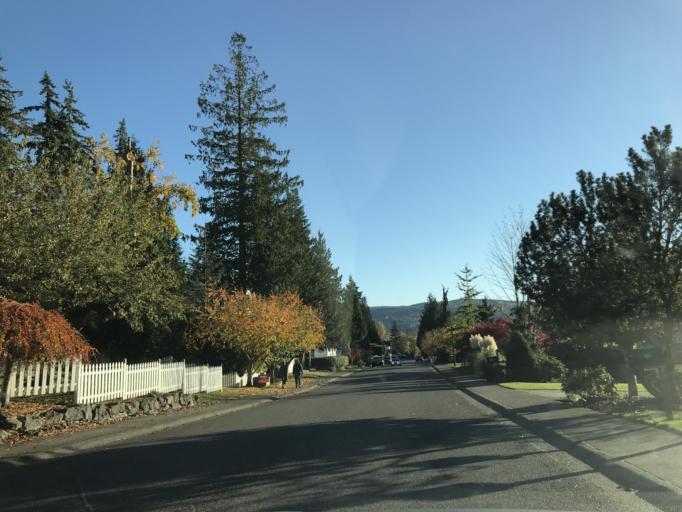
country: US
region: Washington
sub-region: Whatcom County
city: Geneva
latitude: 48.7703
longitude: -122.4031
